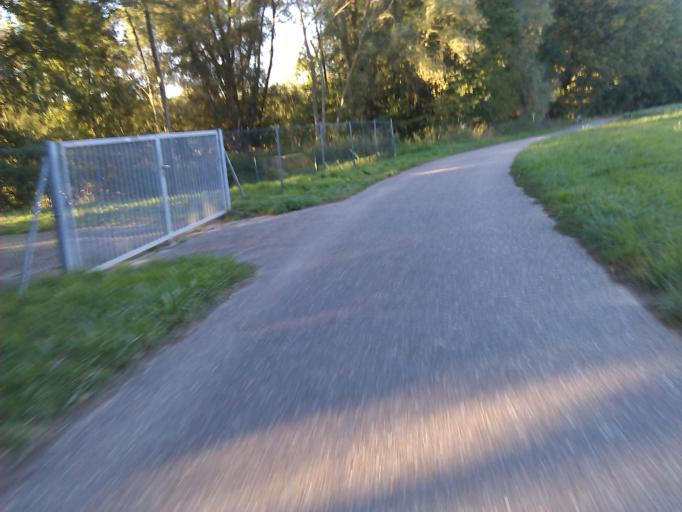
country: DE
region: Baden-Wuerttemberg
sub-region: Regierungsbezirk Stuttgart
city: Ittlingen
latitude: 49.1749
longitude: 8.9347
